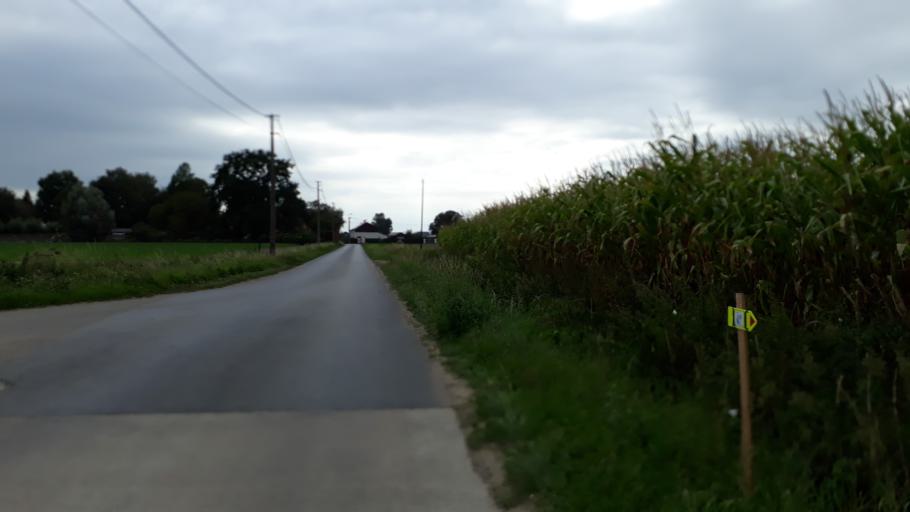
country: BE
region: Flanders
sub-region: Provincie West-Vlaanderen
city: Torhout
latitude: 51.0426
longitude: 3.1202
